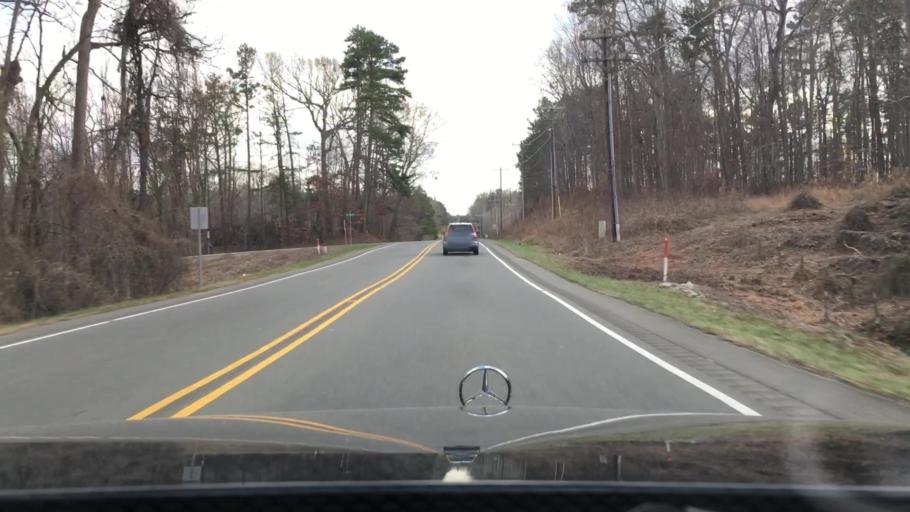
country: US
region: North Carolina
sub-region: Orange County
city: Hillsborough
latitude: 36.1014
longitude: -79.1078
